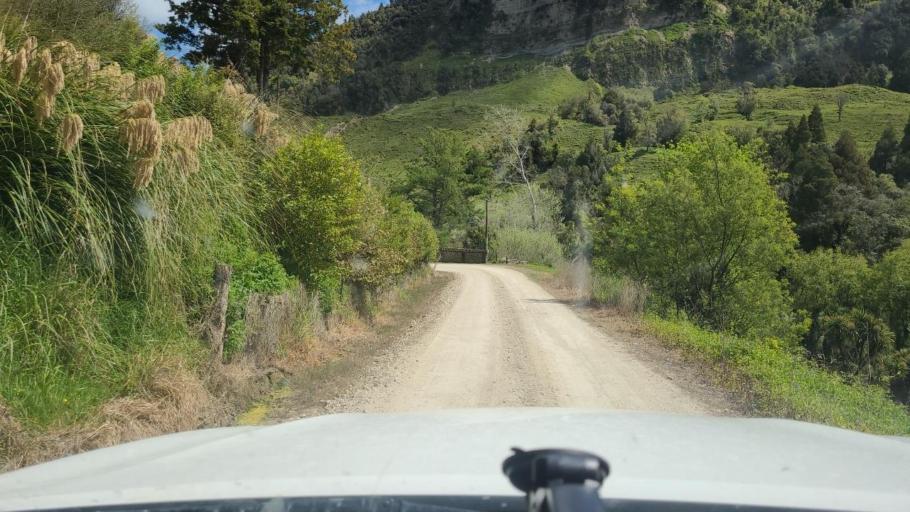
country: NZ
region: Hawke's Bay
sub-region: Wairoa District
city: Wairoa
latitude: -38.8459
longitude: 177.6833
